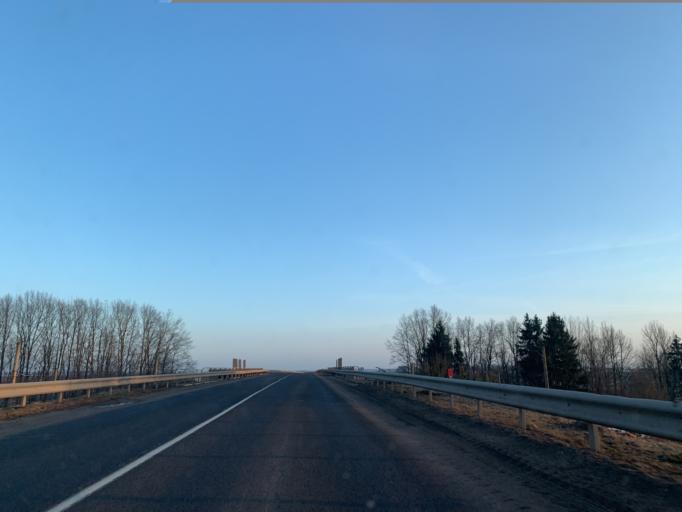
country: BY
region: Minsk
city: Haradzyeya
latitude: 53.3303
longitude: 26.5478
